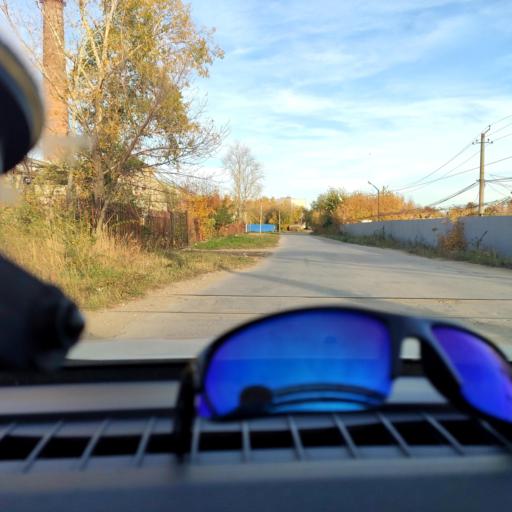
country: RU
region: Samara
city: Chapayevsk
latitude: 52.9938
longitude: 49.7835
